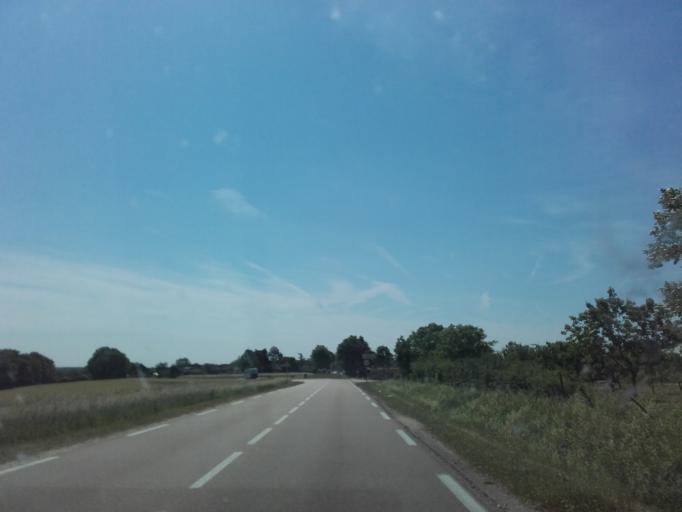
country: FR
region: Bourgogne
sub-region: Departement de l'Yonne
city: Chablis
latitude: 47.7318
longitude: 3.8495
